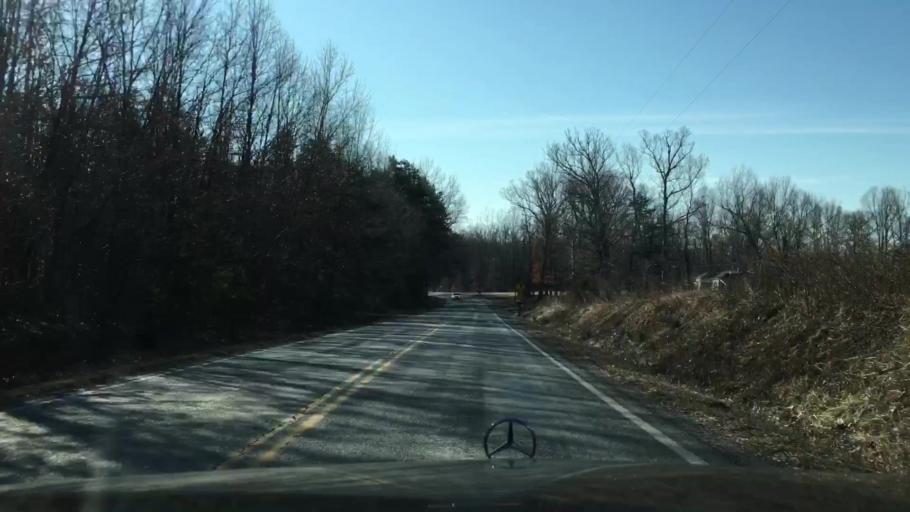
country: US
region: Virginia
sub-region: Pittsylvania County
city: Motley
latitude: 37.1746
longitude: -79.4082
